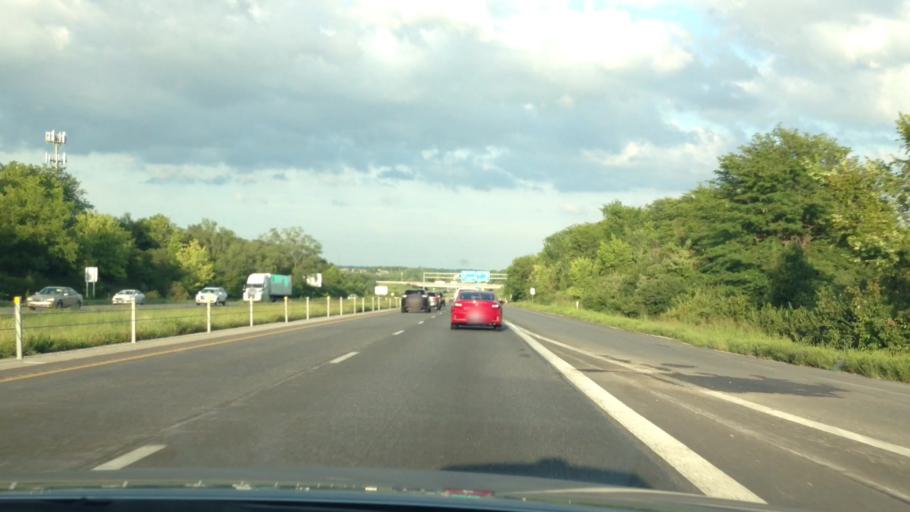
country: US
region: Missouri
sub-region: Clay County
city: Pleasant Valley
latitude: 39.2425
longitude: -94.5172
